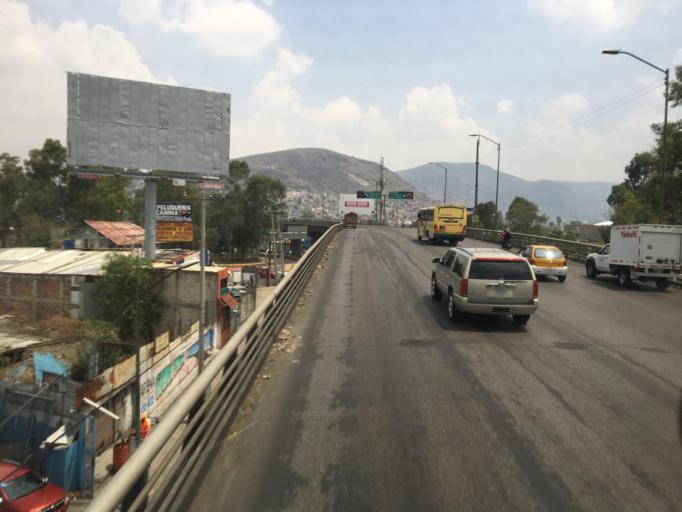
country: MX
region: Mexico
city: Tlalnepantla
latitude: 19.5257
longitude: -99.1588
